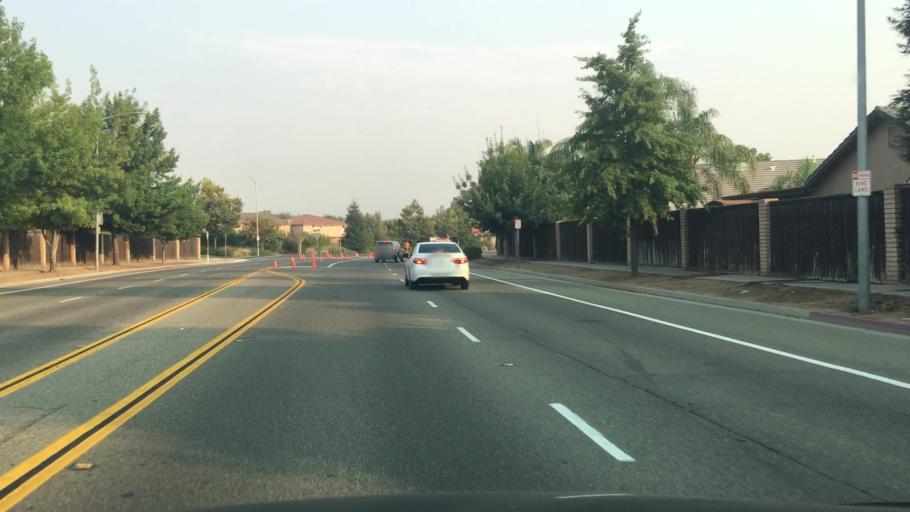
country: US
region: California
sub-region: Fresno County
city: Clovis
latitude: 36.8354
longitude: -119.6743
